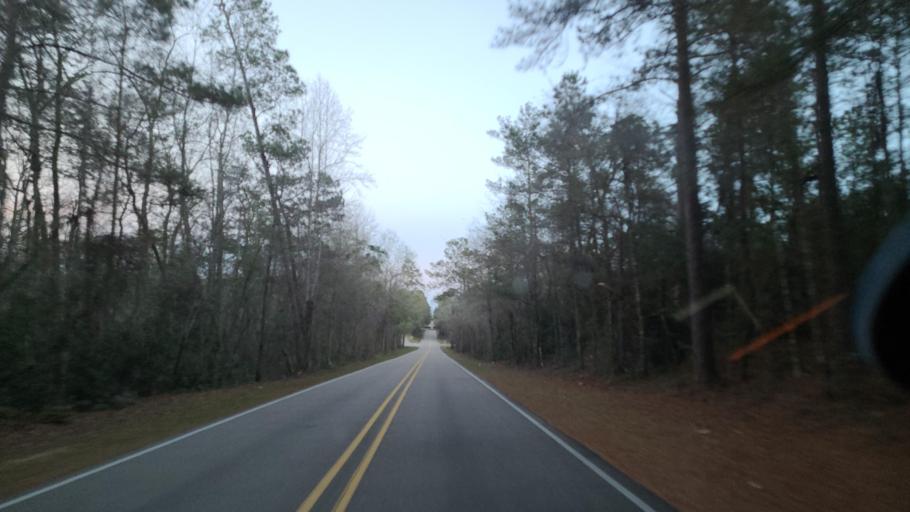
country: US
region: Mississippi
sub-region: Forrest County
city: Hattiesburg
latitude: 31.2116
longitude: -89.2564
